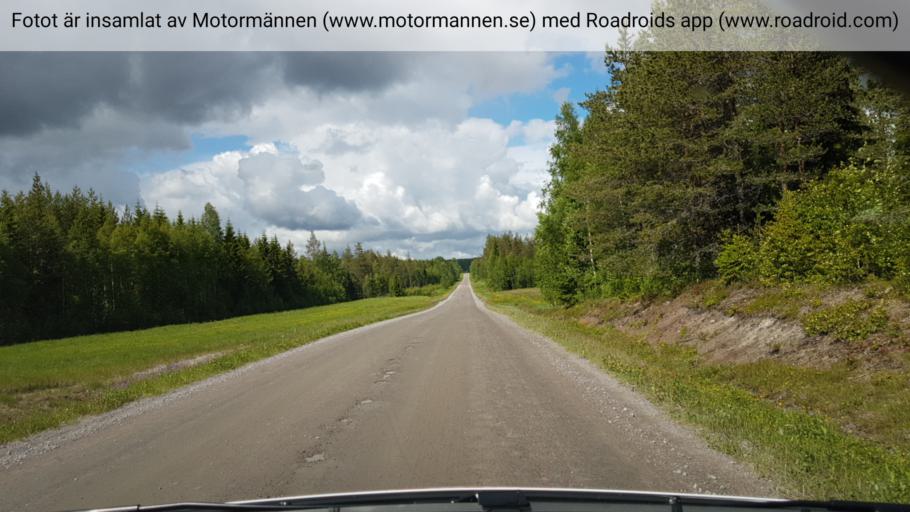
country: SE
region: Vaesterbotten
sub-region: Vannas Kommun
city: Vannasby
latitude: 63.8231
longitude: 19.9860
